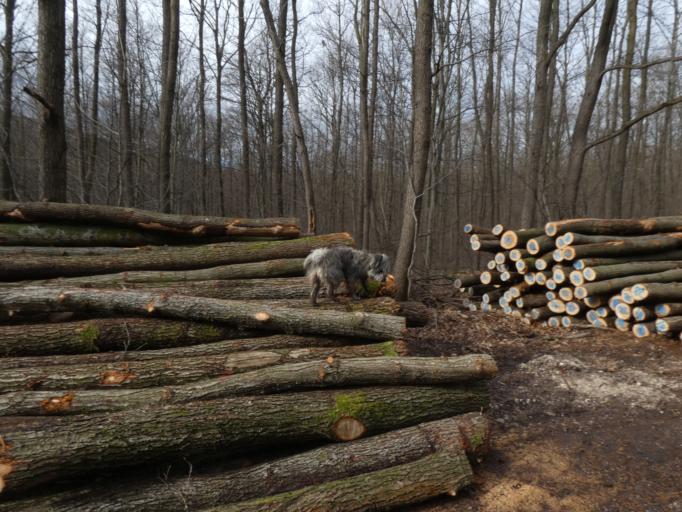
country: HU
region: Pest
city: Pilisszentkereszt
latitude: 47.7205
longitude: 18.9328
